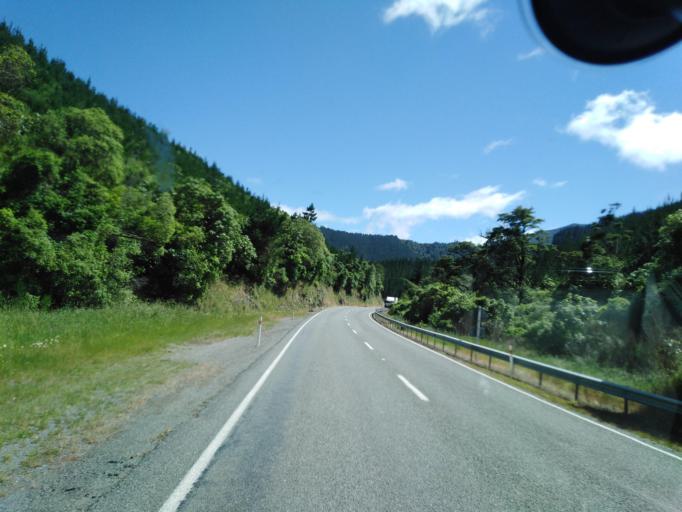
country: NZ
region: Nelson
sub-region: Nelson City
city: Nelson
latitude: -41.1741
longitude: 173.5630
